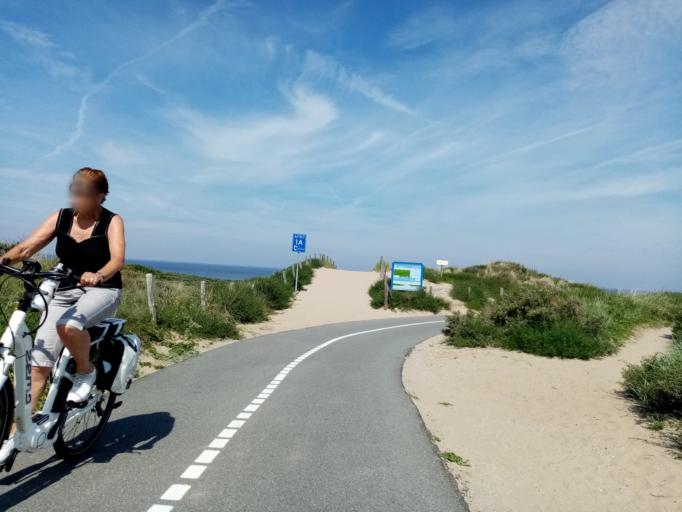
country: NL
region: South Holland
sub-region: Gemeente Noordwijk
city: Noordwijk-Binnen
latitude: 52.2297
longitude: 4.4179
